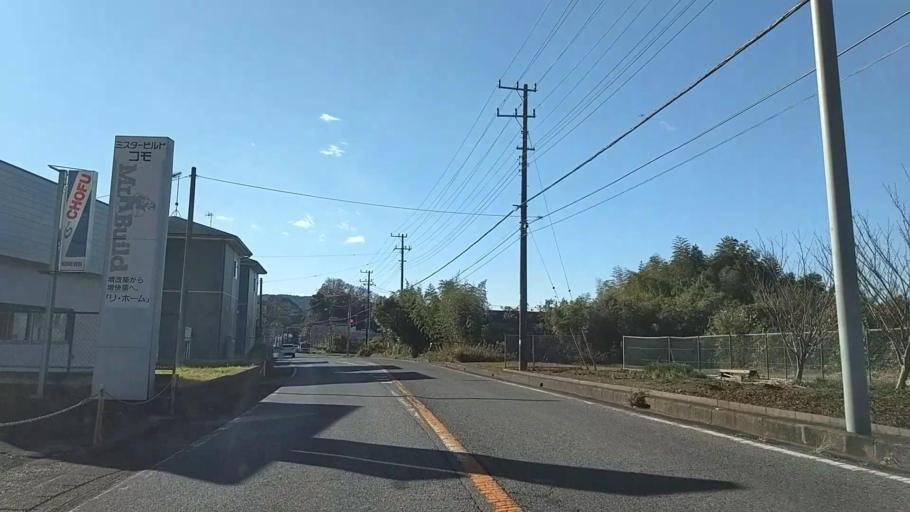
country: JP
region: Chiba
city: Futtsu
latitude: 35.2277
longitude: 139.8740
